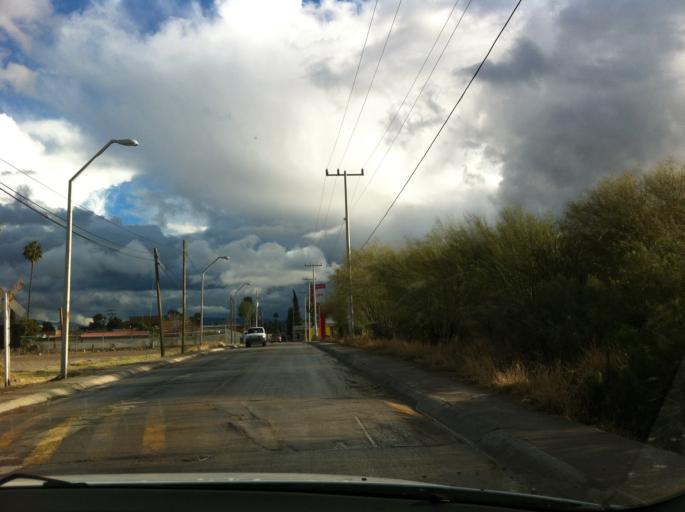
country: MX
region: Sonora
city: Magdalena de Kino
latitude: 30.6282
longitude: -110.9772
